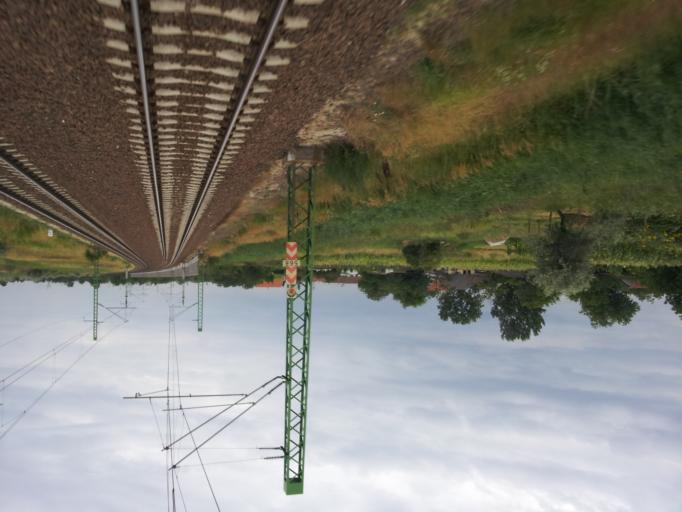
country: HU
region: Fejer
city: Pakozd
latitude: 47.1791
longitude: 18.5596
